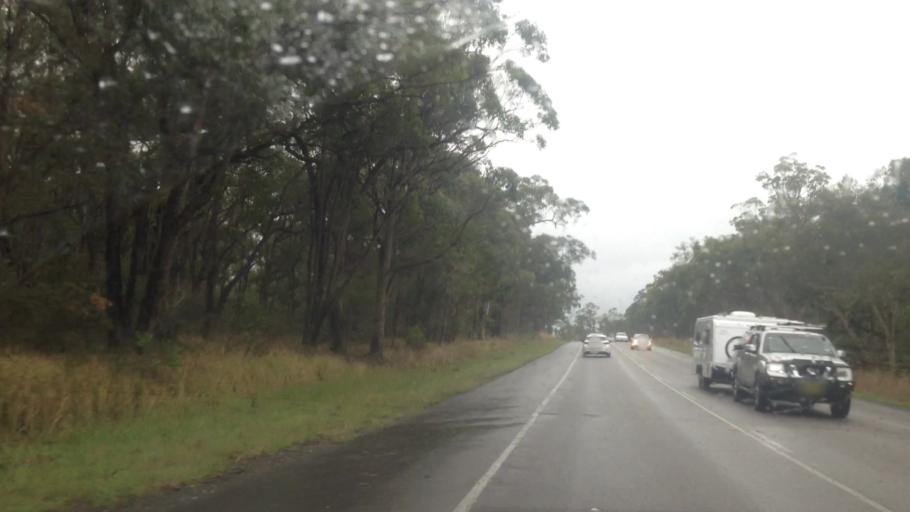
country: AU
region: New South Wales
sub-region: Lake Macquarie Shire
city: Dora Creek
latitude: -33.1314
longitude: 151.4766
